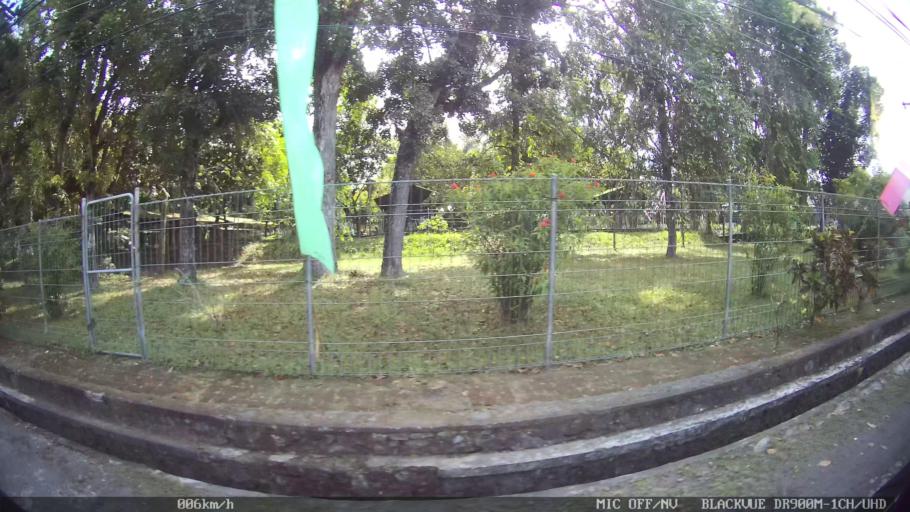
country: ID
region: Daerah Istimewa Yogyakarta
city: Depok
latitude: -7.7540
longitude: 110.4231
